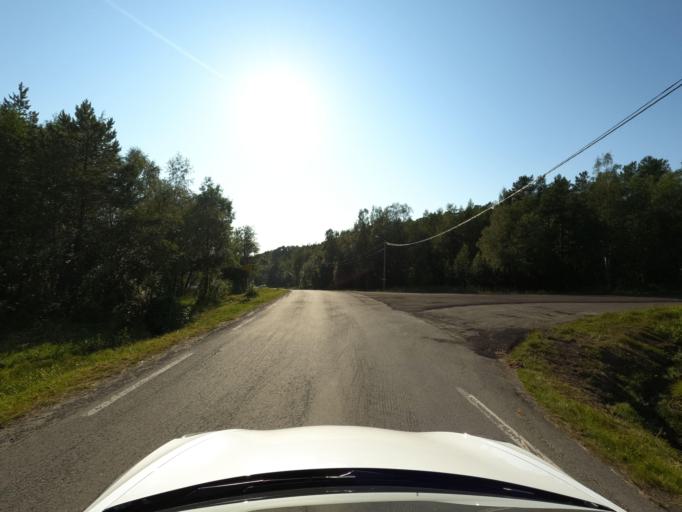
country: NO
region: Nordland
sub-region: Narvik
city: Bjerkvik
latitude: 68.4761
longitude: 17.5179
